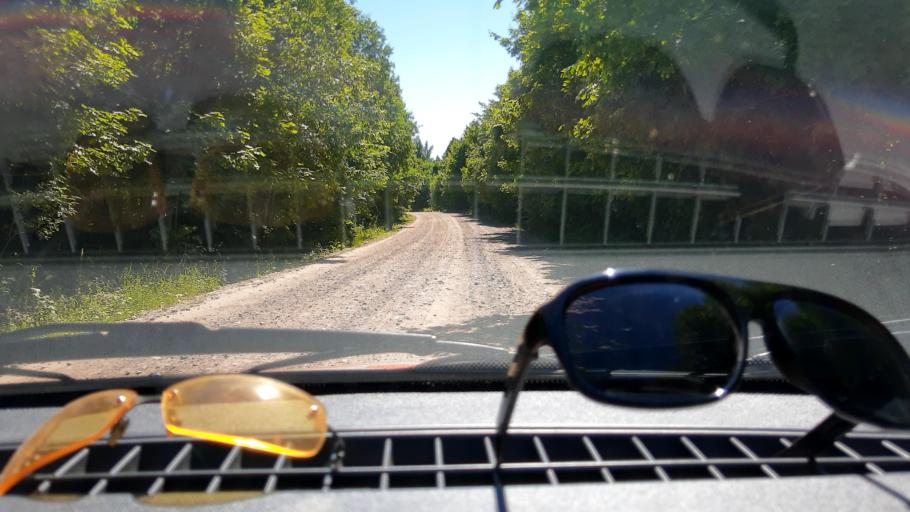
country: RU
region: Bashkortostan
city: Ulu-Telyak
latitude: 54.8005
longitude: 57.0284
